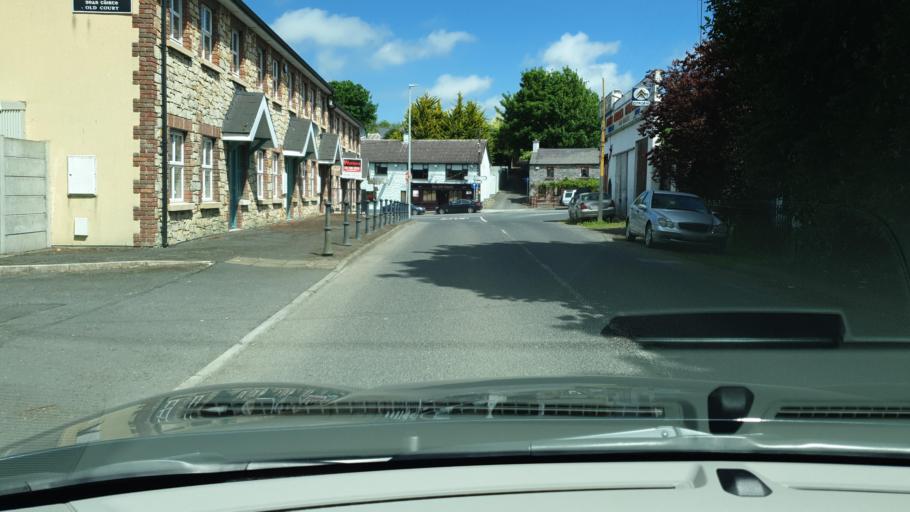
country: IE
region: Leinster
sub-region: Lu
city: Ardee
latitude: 53.8496
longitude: -6.6538
